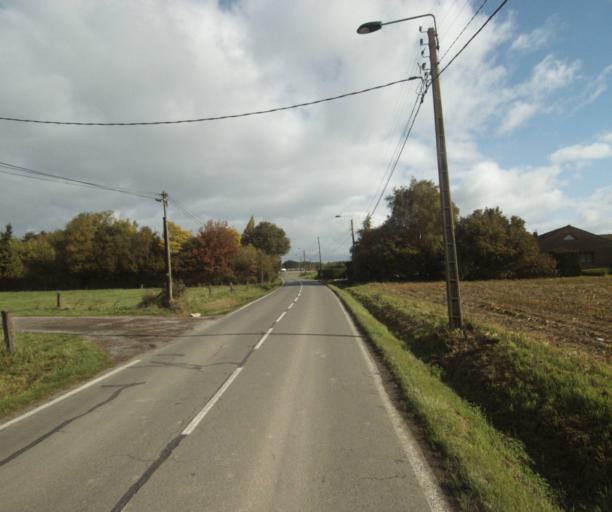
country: FR
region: Nord-Pas-de-Calais
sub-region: Departement du Nord
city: Verlinghem
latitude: 50.6875
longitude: 3.0081
